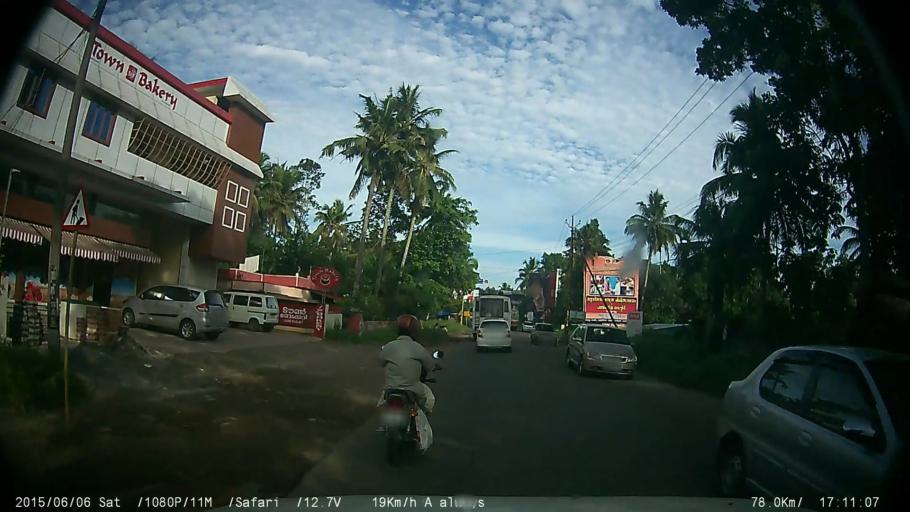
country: IN
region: Kerala
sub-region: Pattanamtitta
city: Tiruvalla
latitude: 9.4055
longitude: 76.5600
